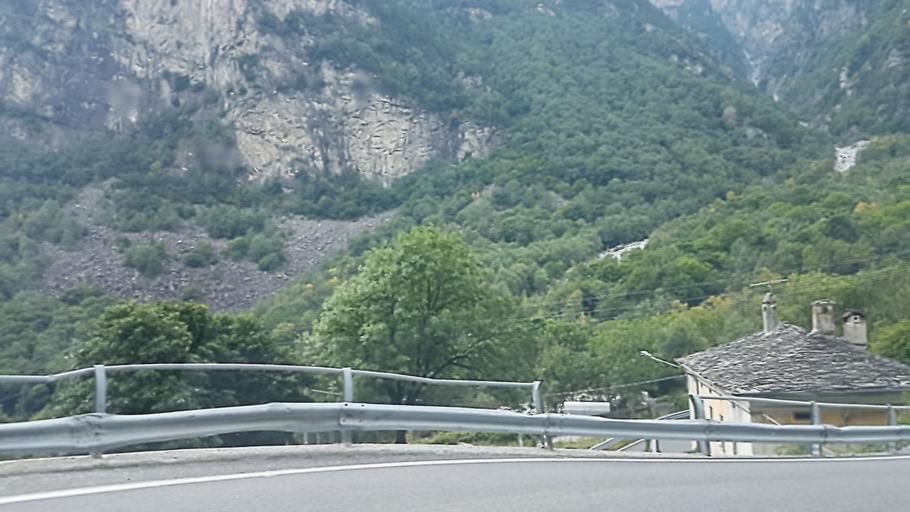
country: IT
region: Lombardy
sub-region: Provincia di Sondrio
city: San Giacomo Filippo
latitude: 46.3638
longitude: 9.3648
